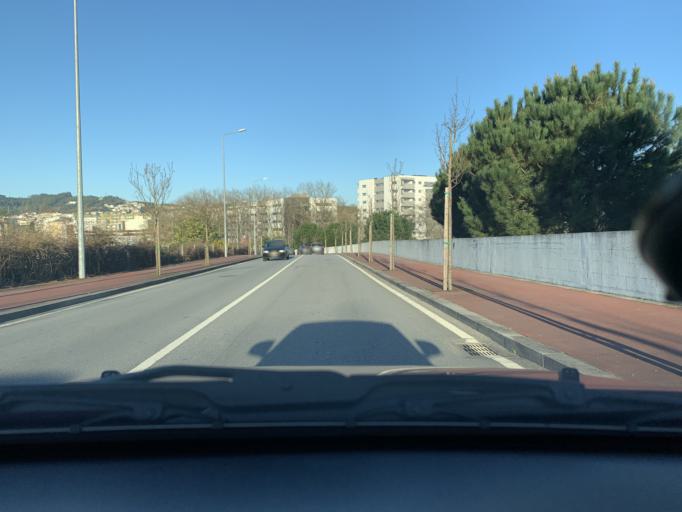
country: PT
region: Braga
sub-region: Vila Nova de Famalicao
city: Vila Nova de Famalicao
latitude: 41.4029
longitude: -8.5134
